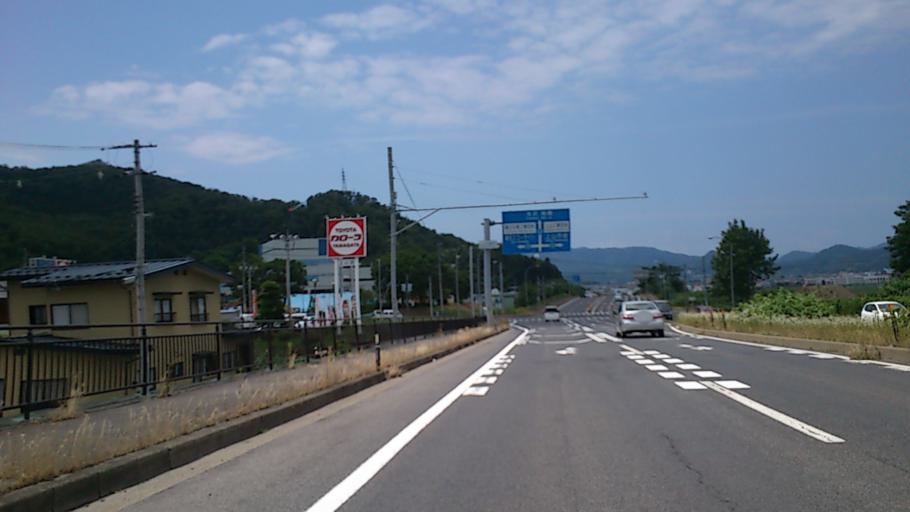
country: JP
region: Yamagata
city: Kaminoyama
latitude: 38.1648
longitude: 140.3055
